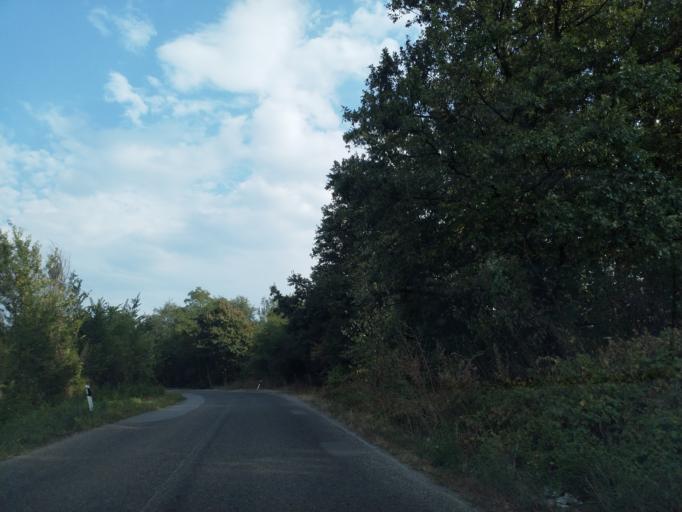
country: RS
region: Central Serbia
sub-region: Pomoravski Okrug
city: Paracin
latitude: 43.8507
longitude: 21.4466
